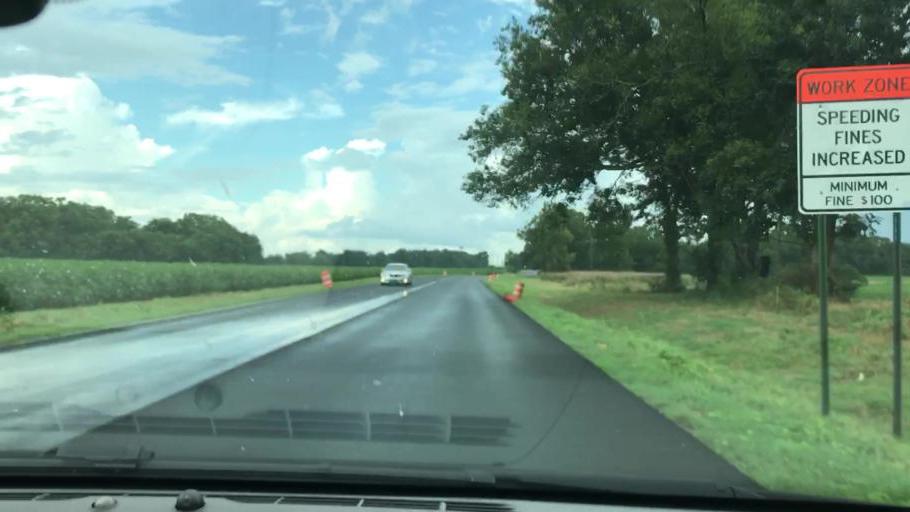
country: US
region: Georgia
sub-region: Early County
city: Blakely
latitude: 31.4298
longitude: -84.9704
